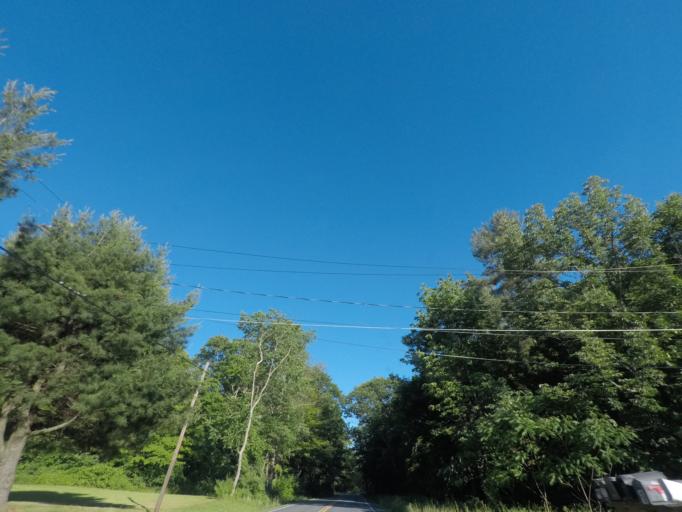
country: US
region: New York
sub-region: Rensselaer County
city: Averill Park
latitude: 42.5910
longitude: -73.5832
